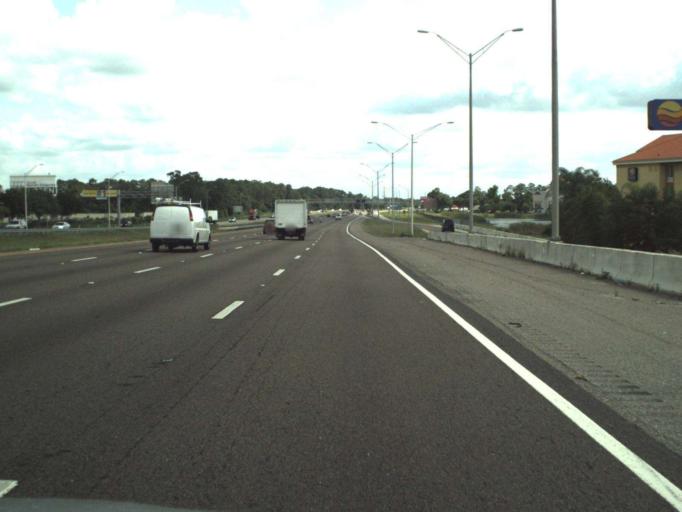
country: US
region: Florida
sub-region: Seminole County
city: Lake Mary
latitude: 28.8140
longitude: -81.3363
